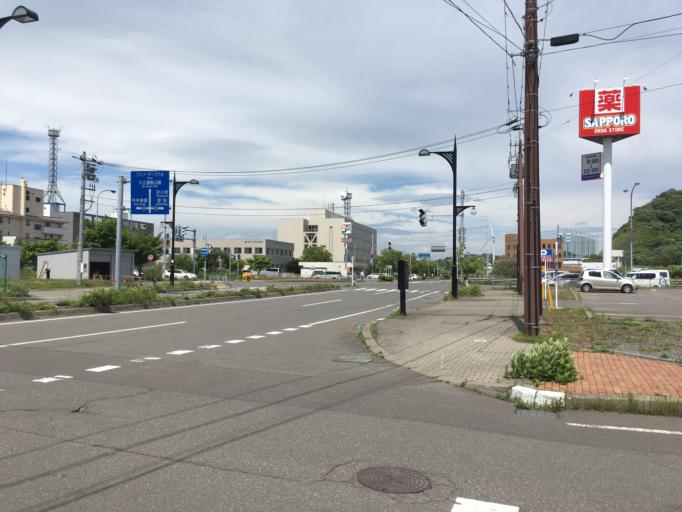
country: JP
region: Hokkaido
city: Muroran
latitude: 42.3198
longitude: 140.9727
